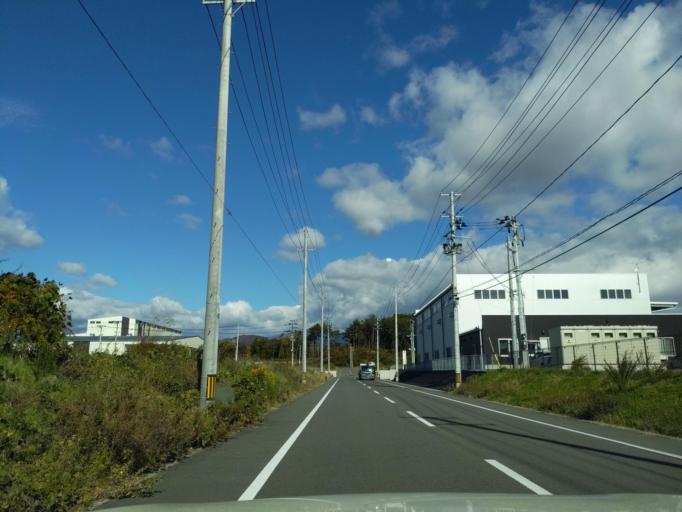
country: JP
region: Fukushima
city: Koriyama
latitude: 37.4629
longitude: 140.3019
